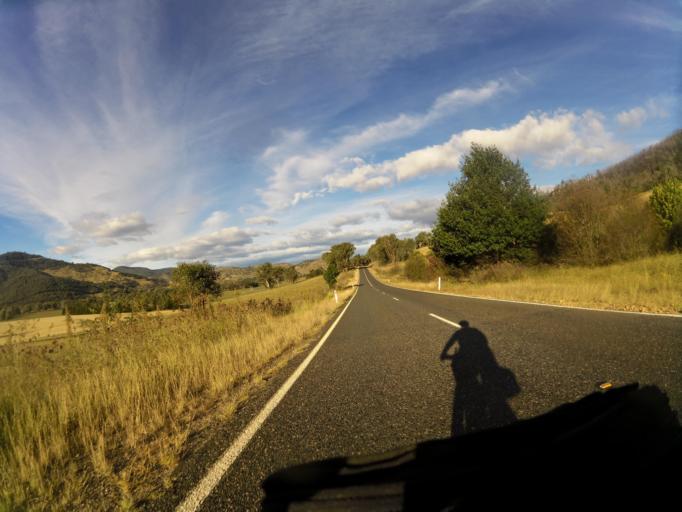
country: AU
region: New South Wales
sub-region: Greater Hume Shire
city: Holbrook
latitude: -36.0065
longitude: 147.8934
